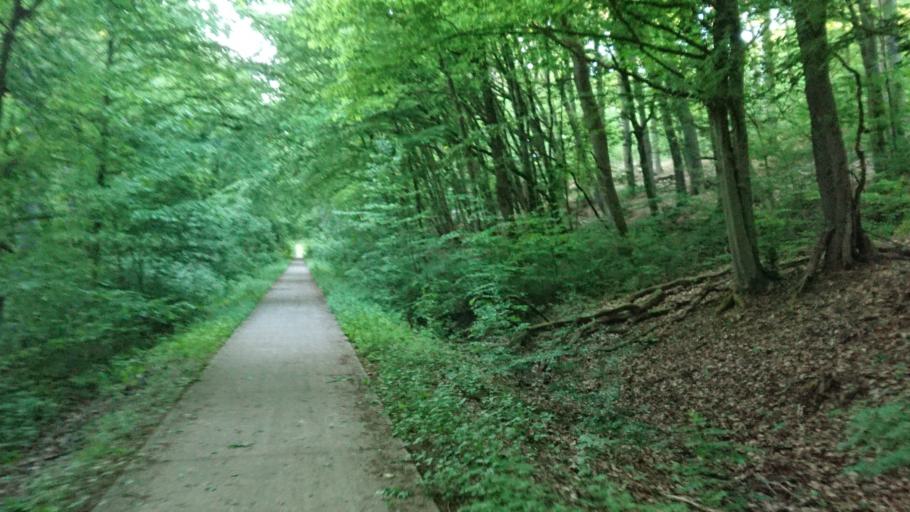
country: DE
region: Lower Saxony
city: Scheden
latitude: 51.4767
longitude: 9.7271
